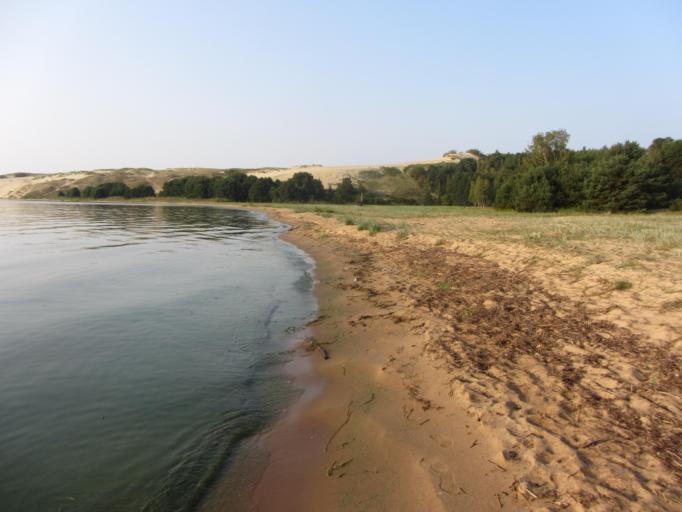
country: LT
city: Nida
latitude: 55.2984
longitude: 20.9990
